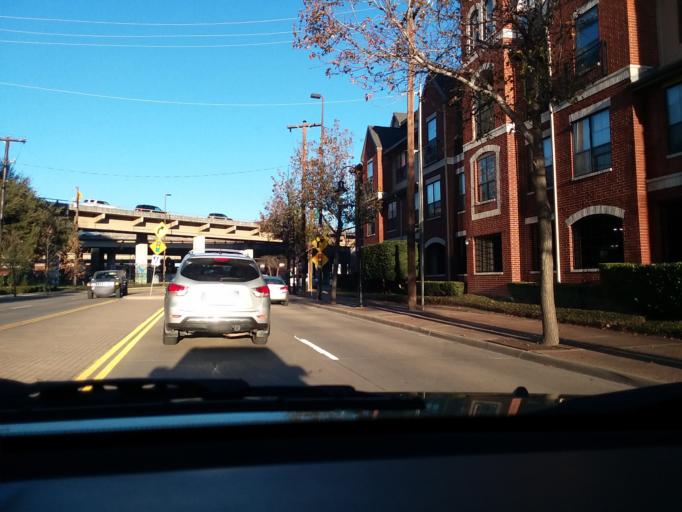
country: US
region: Texas
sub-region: Dallas County
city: Dallas
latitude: 32.7815
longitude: -96.7879
